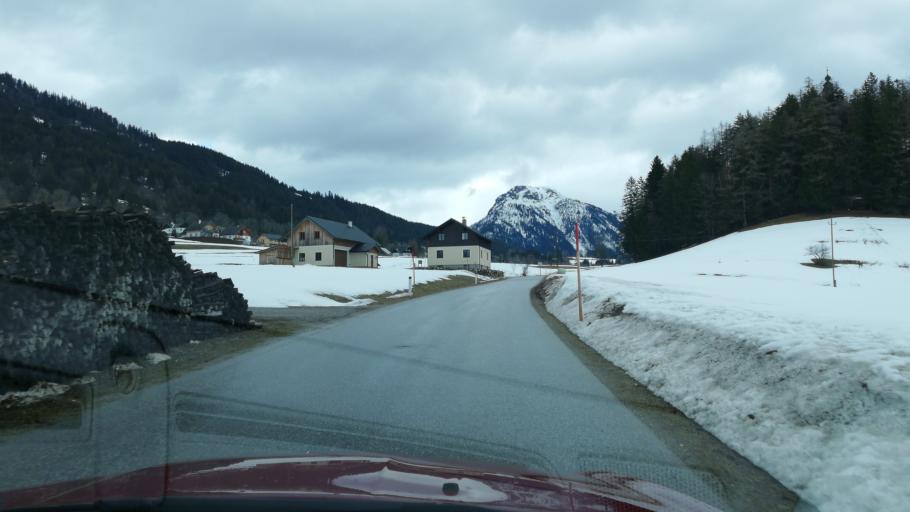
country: AT
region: Styria
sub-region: Politischer Bezirk Liezen
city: Bad Aussee
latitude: 47.5688
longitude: 13.8785
